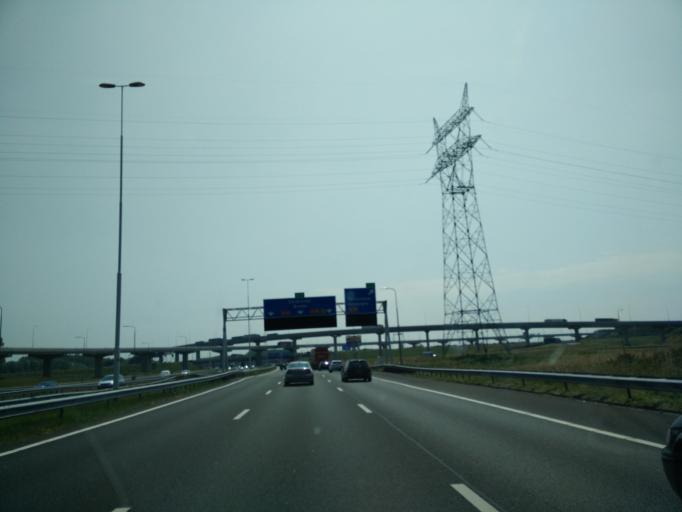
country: NL
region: South Holland
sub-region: Gemeente Ridderkerk
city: Ridderkerk
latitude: 51.8782
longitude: 4.5674
